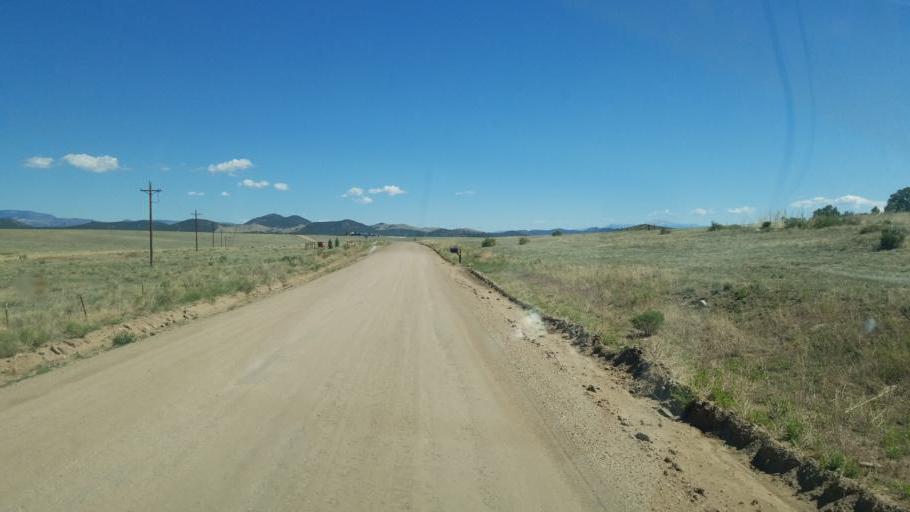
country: US
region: Colorado
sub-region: Custer County
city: Westcliffe
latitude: 38.2482
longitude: -105.5005
